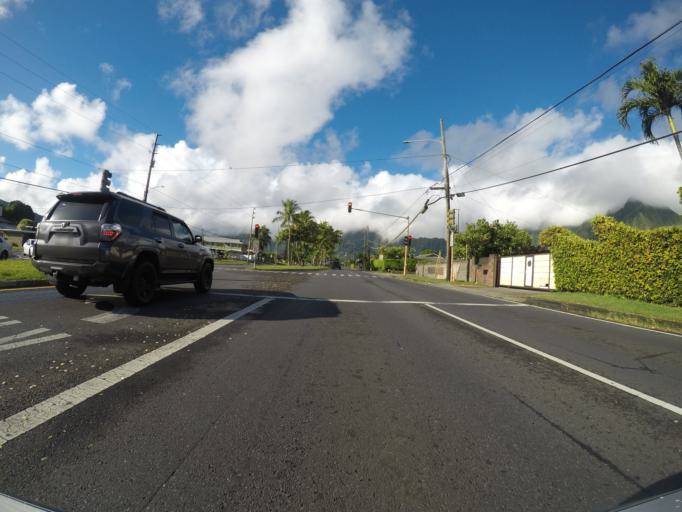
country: US
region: Hawaii
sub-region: Honolulu County
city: Kane'ohe
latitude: 21.4096
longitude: -157.7993
